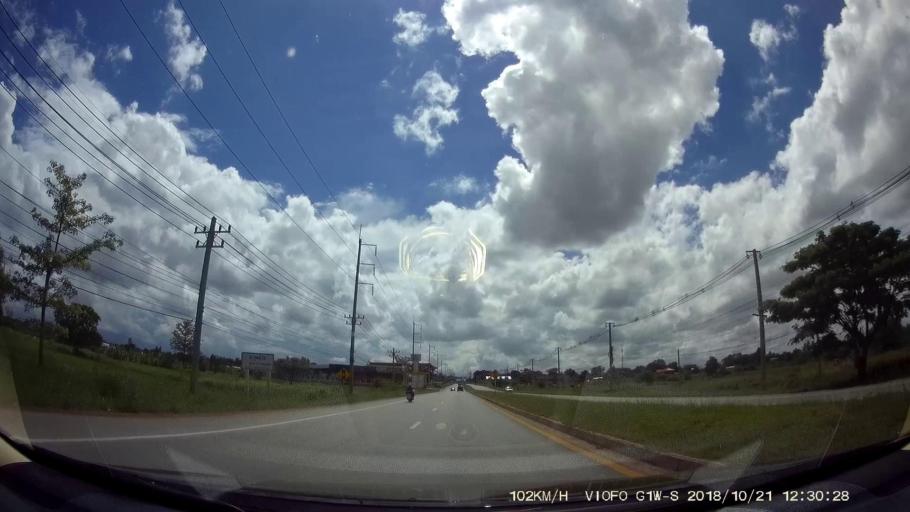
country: TH
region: Nakhon Ratchasima
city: Dan Khun Thot
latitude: 15.1705
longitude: 101.7391
